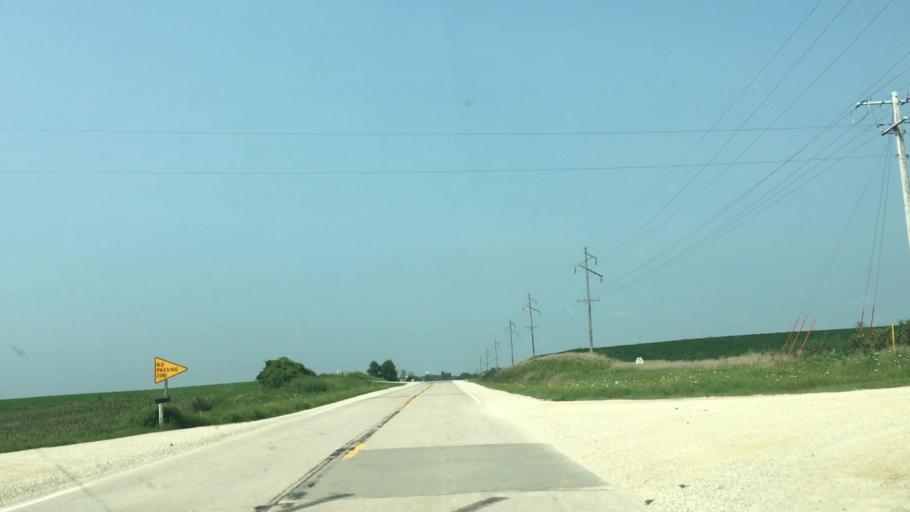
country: US
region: Iowa
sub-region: Winneshiek County
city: Decorah
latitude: 43.1473
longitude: -91.8643
